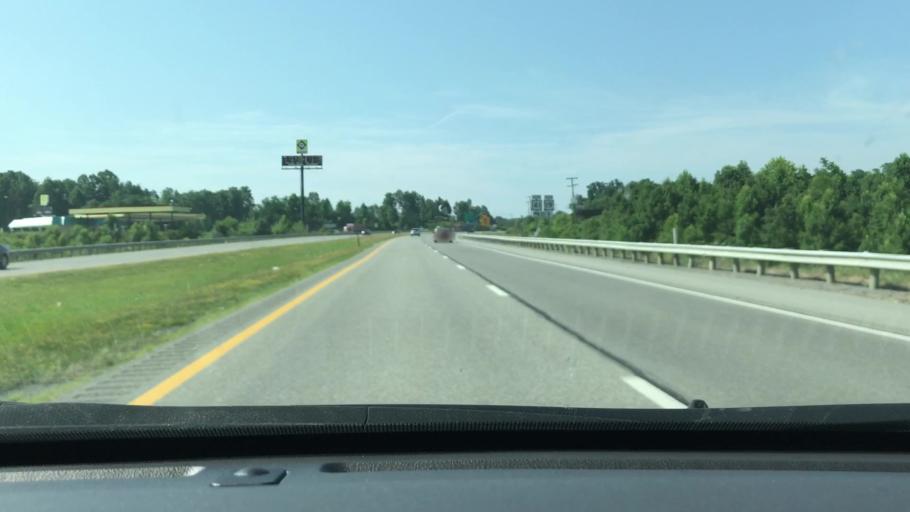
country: US
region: West Virginia
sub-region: Nicholas County
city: Summersville
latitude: 38.2142
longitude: -80.8527
